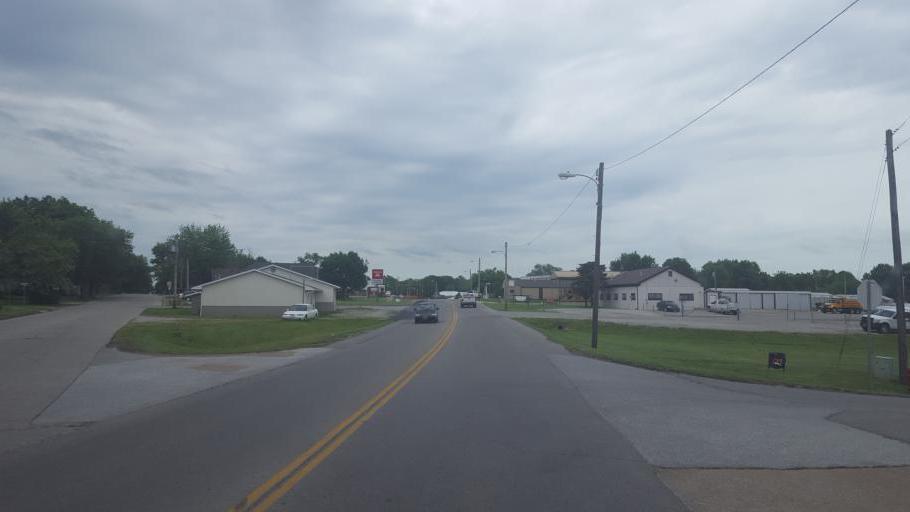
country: US
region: Missouri
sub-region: Moniteau County
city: California
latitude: 38.6289
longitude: -92.5773
